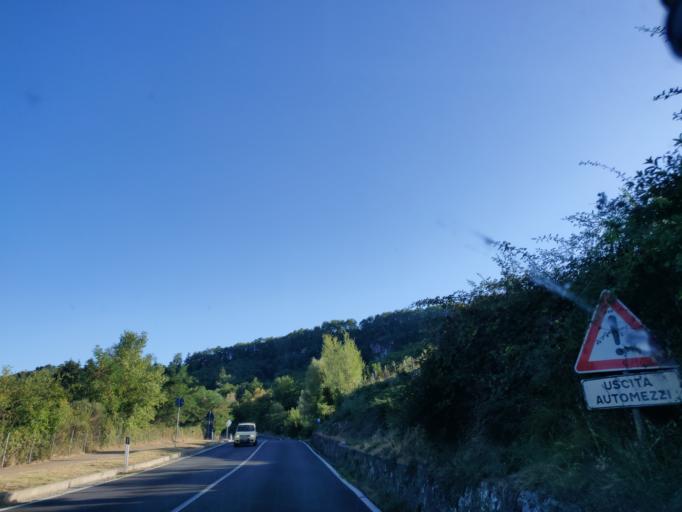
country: IT
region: Tuscany
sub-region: Provincia di Siena
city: Piancastagnaio
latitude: 42.8643
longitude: 11.6788
